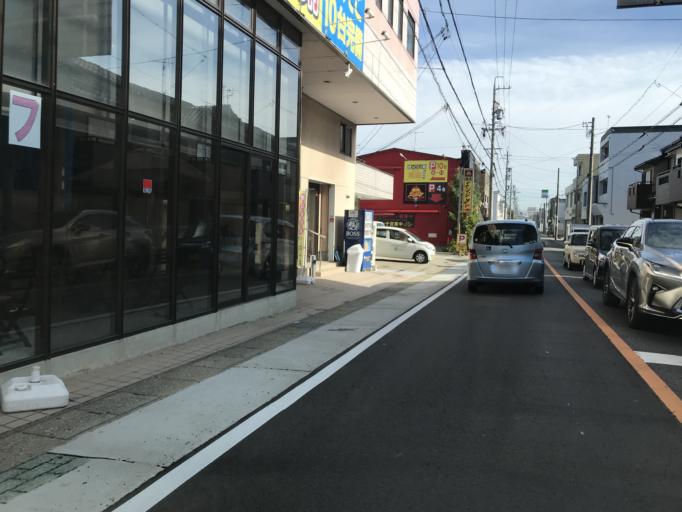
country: JP
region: Aichi
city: Nagoya-shi
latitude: 35.2204
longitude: 136.9334
